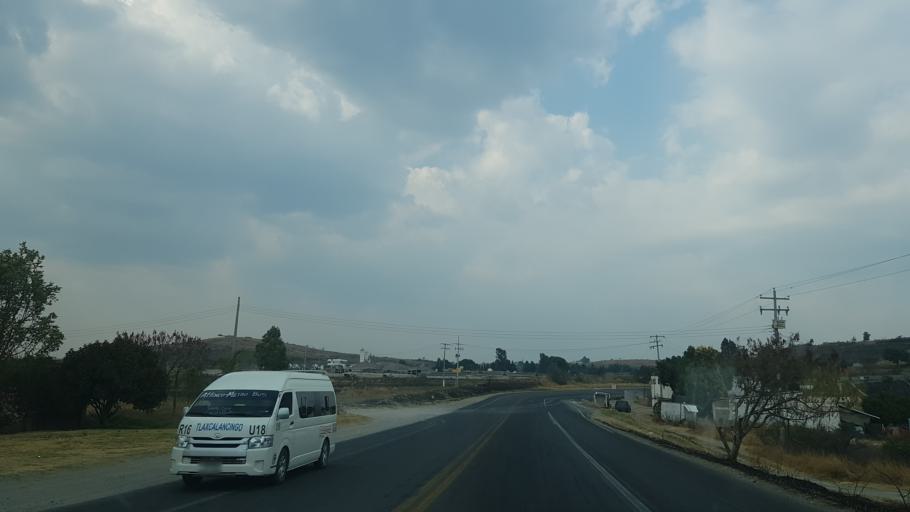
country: MX
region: Puebla
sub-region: Santa Isabel Cholula
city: San Martin Tlamapa
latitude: 18.9729
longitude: -98.3810
